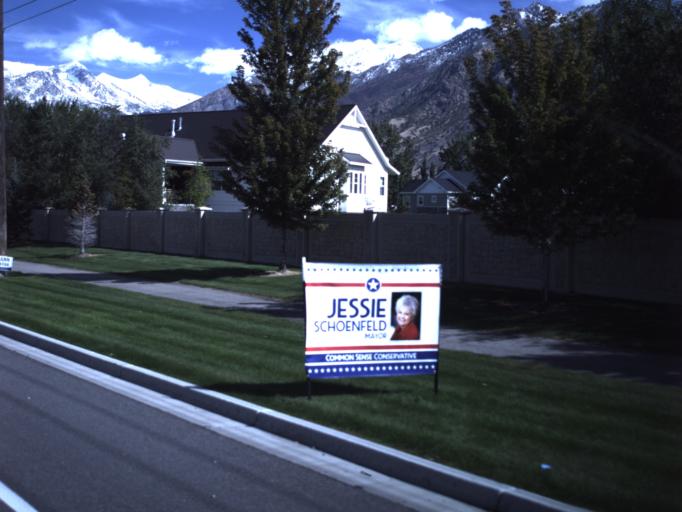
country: US
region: Utah
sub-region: Utah County
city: Cedar Hills
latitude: 40.4234
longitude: -111.7734
